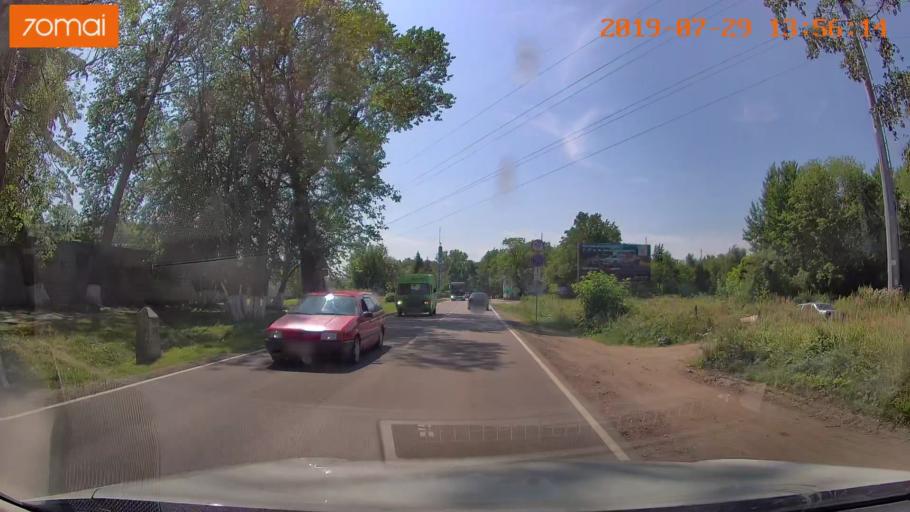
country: RU
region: Kaliningrad
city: Primorsk
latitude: 54.7096
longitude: 19.9506
